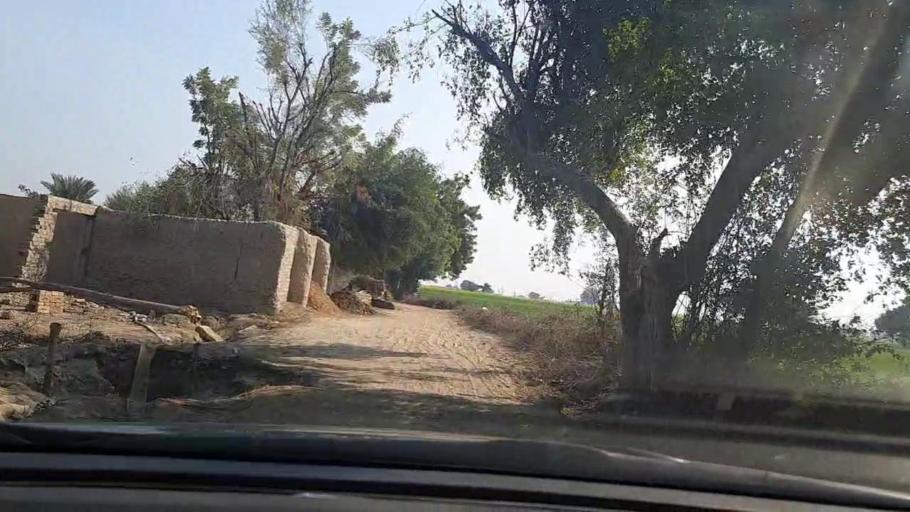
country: PK
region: Sindh
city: Sann
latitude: 26.2655
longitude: 68.0727
